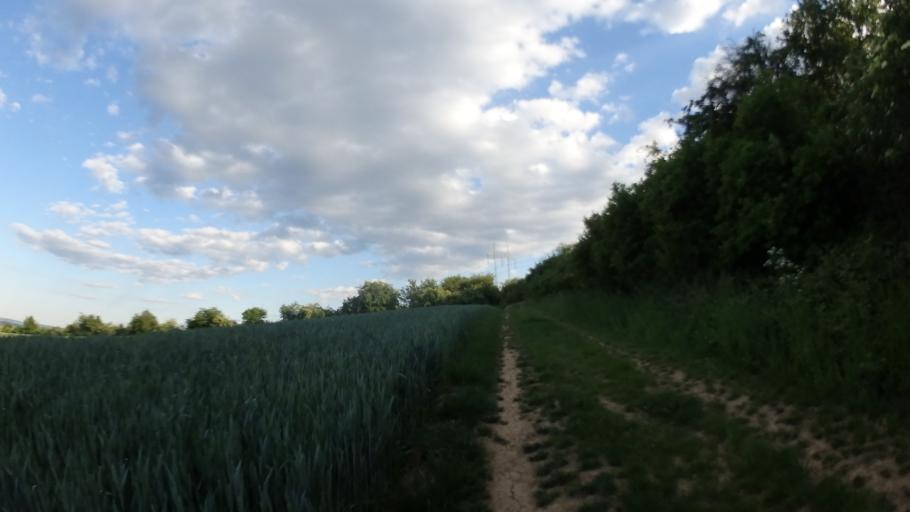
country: CZ
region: South Moravian
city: Zelesice
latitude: 49.1301
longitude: 16.5895
